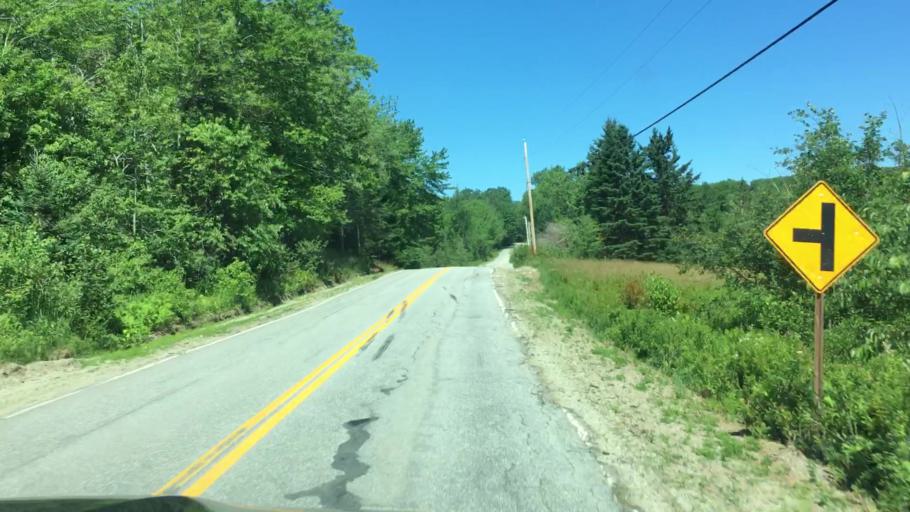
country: US
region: Maine
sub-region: Hancock County
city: Penobscot
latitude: 44.4251
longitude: -68.7091
